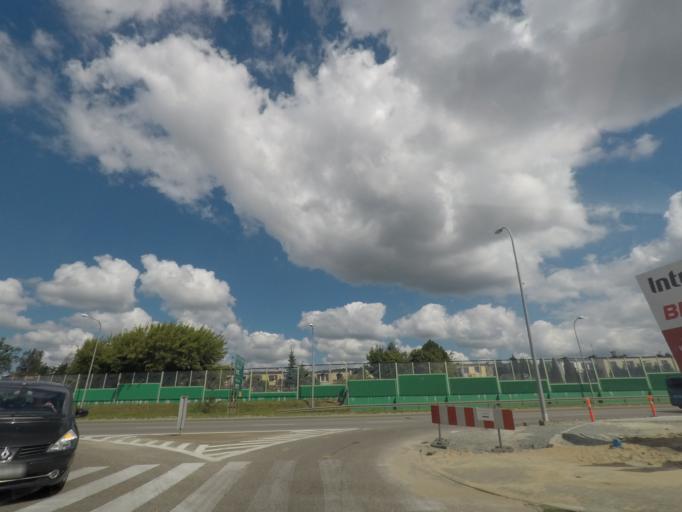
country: PL
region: Pomeranian Voivodeship
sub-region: Powiat wejherowski
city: Wejherowo
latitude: 54.6073
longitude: 18.2256
